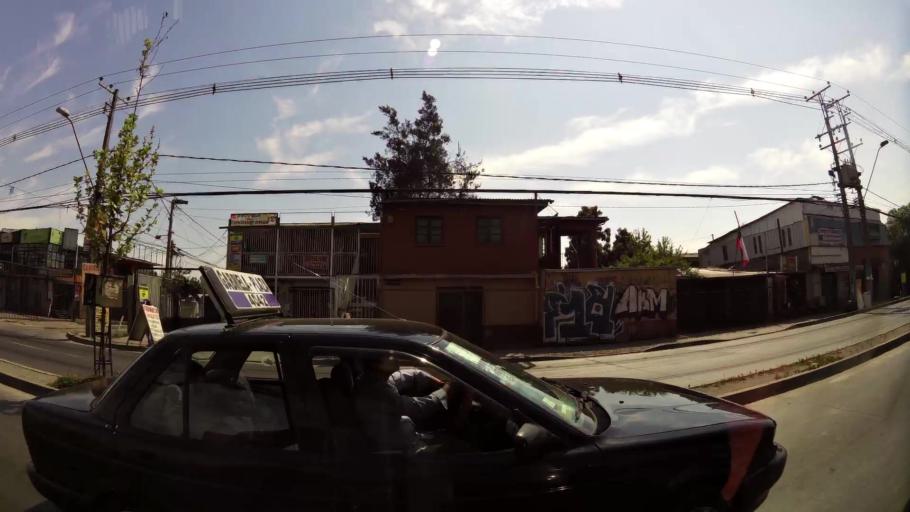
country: CL
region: Santiago Metropolitan
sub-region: Provincia de Cordillera
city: Puente Alto
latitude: -33.5799
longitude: -70.5864
